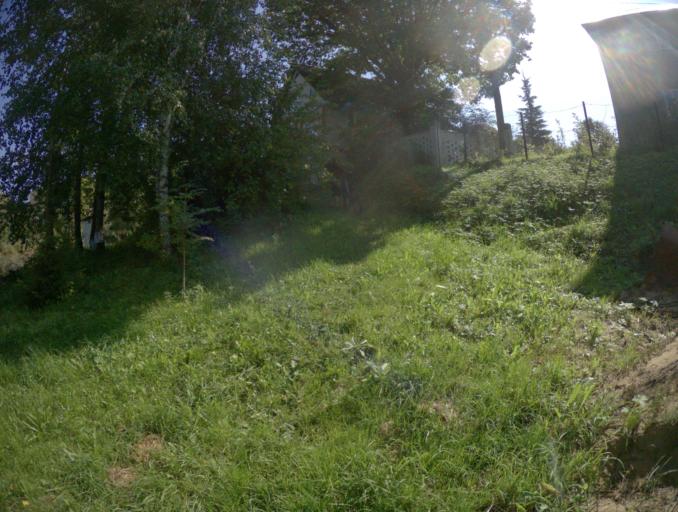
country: RU
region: Vladimir
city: Vladimir
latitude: 56.2534
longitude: 40.4135
